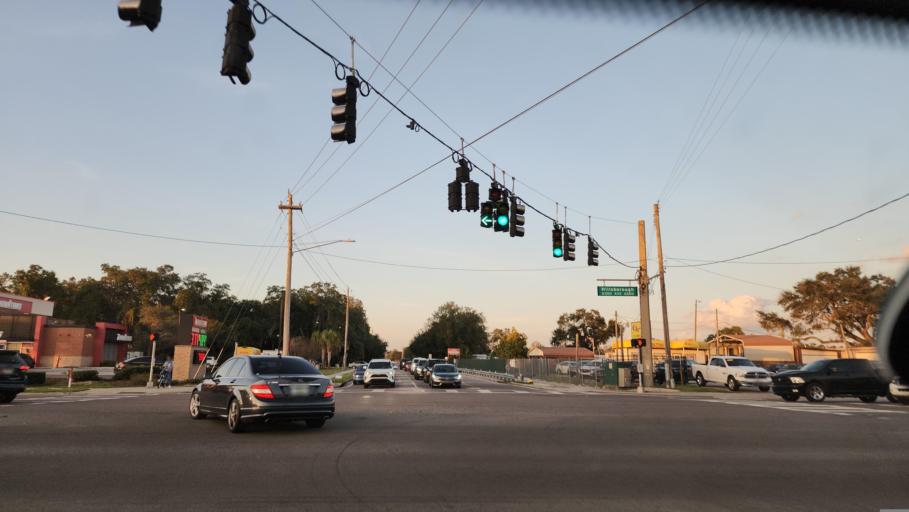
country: US
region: Florida
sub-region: Hillsborough County
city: Town 'n' Country
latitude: 27.9963
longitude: -82.5503
